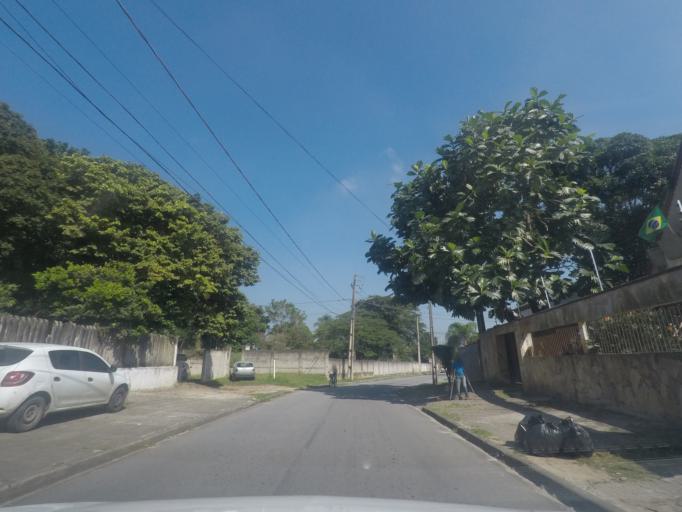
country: BR
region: Parana
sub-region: Paranagua
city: Paranagua
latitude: -25.5294
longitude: -48.5161
